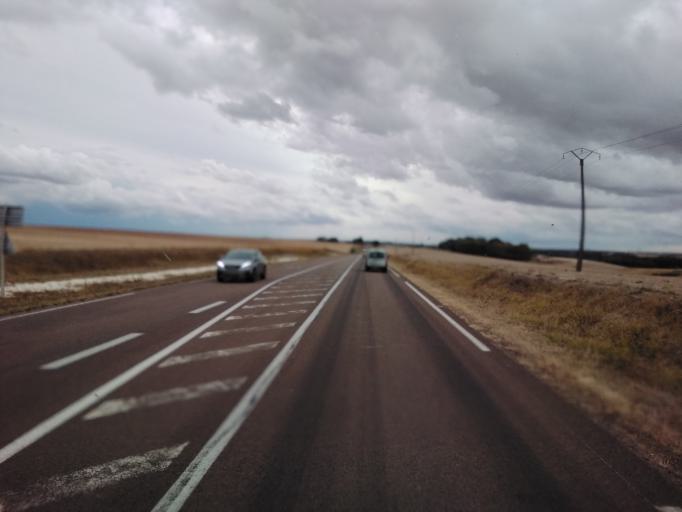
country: FR
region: Champagne-Ardenne
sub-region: Departement de la Marne
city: Frignicourt
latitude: 48.6086
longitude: 4.5546
